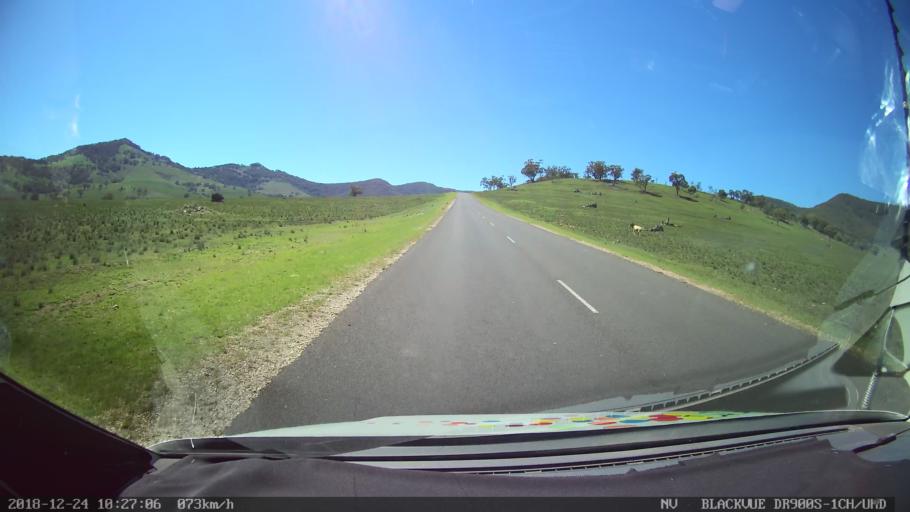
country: AU
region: New South Wales
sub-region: Liverpool Plains
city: Quirindi
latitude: -31.8145
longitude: 150.5301
